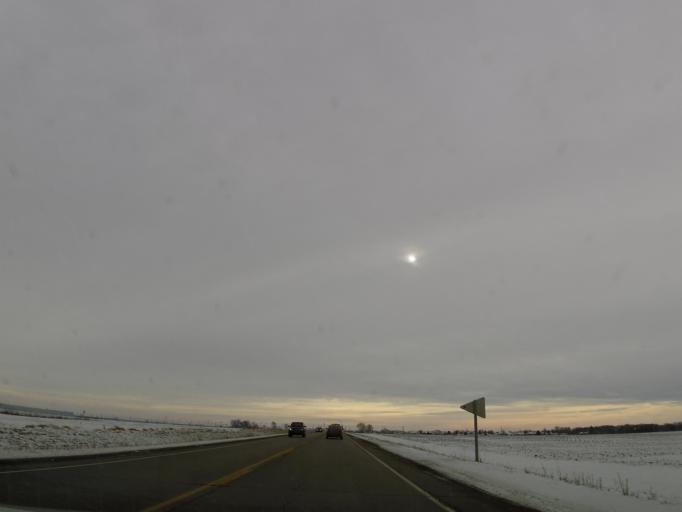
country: US
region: Illinois
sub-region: LaSalle County
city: Peru
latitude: 41.3016
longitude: -89.1074
